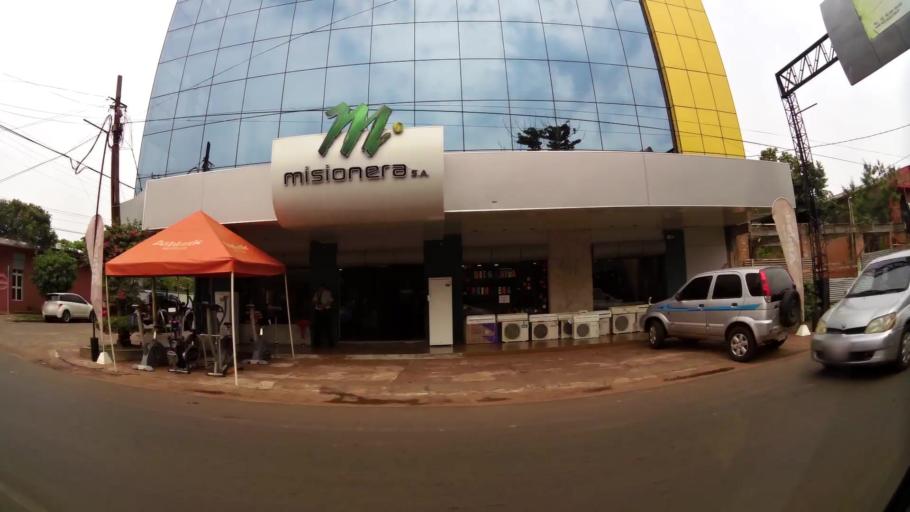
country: BR
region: Parana
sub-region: Foz Do Iguacu
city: Foz do Iguacu
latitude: -25.5615
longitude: -54.6049
